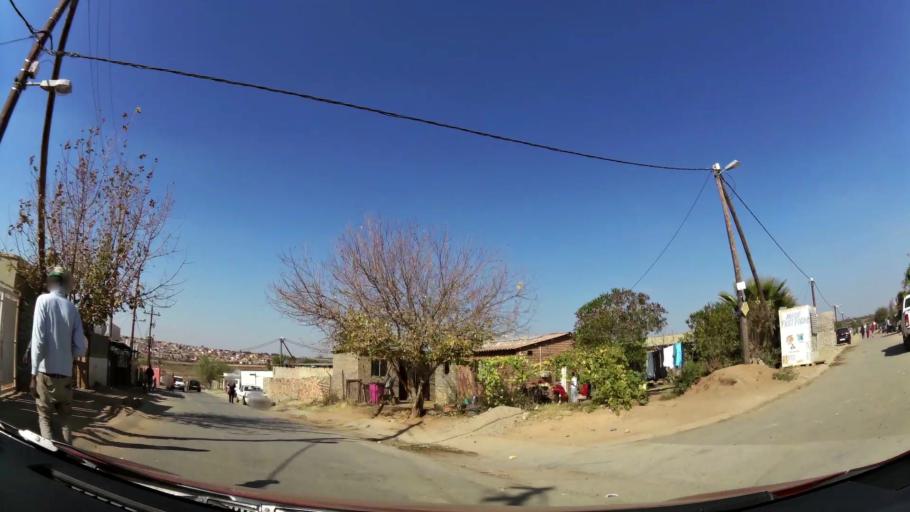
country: ZA
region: Gauteng
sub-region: West Rand District Municipality
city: Muldersdriseloop
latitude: -26.0283
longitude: 27.9286
